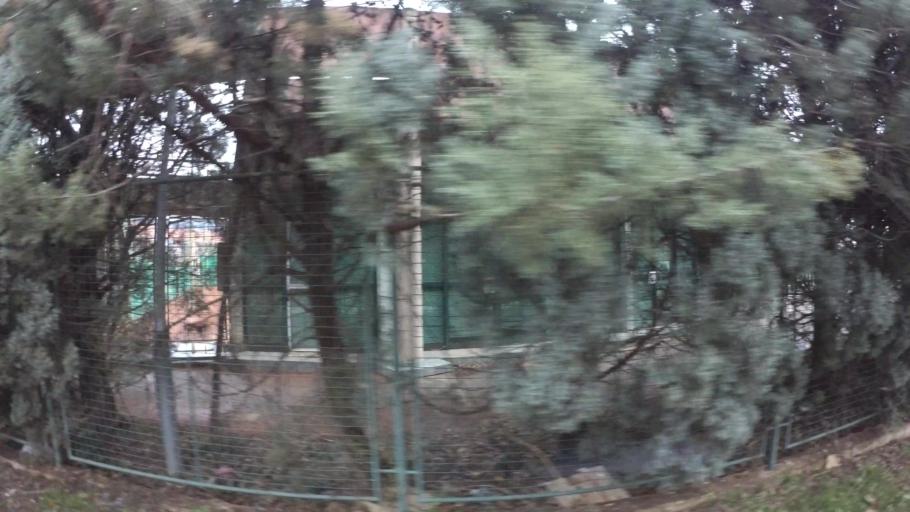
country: BA
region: Federation of Bosnia and Herzegovina
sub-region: Hercegovacko-Bosanski Kanton
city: Mostar
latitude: 43.3394
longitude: 17.8048
